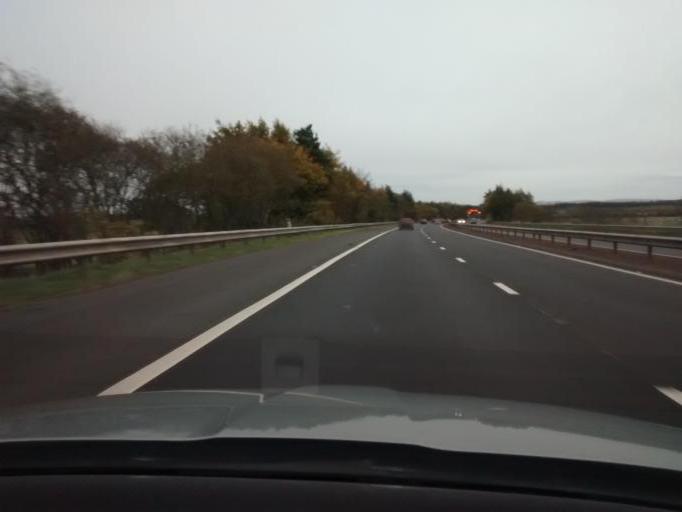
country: GB
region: Scotland
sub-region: Stirling
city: Cowie
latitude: 56.0542
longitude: -3.8429
